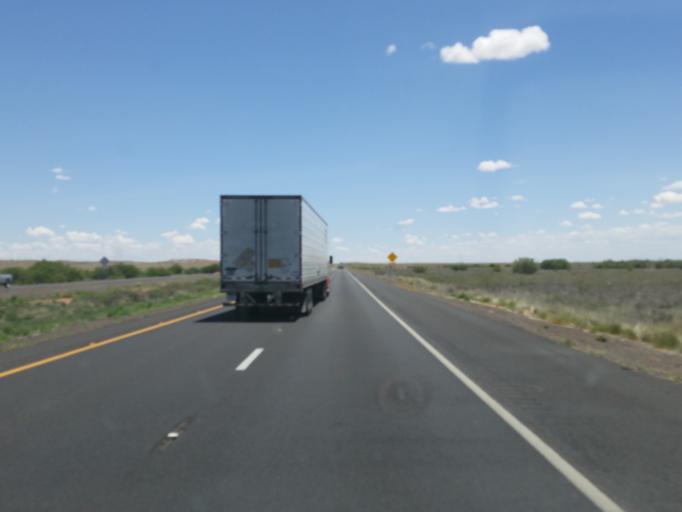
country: US
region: Arizona
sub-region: Navajo County
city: Winslow
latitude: 34.9880
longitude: -110.5636
